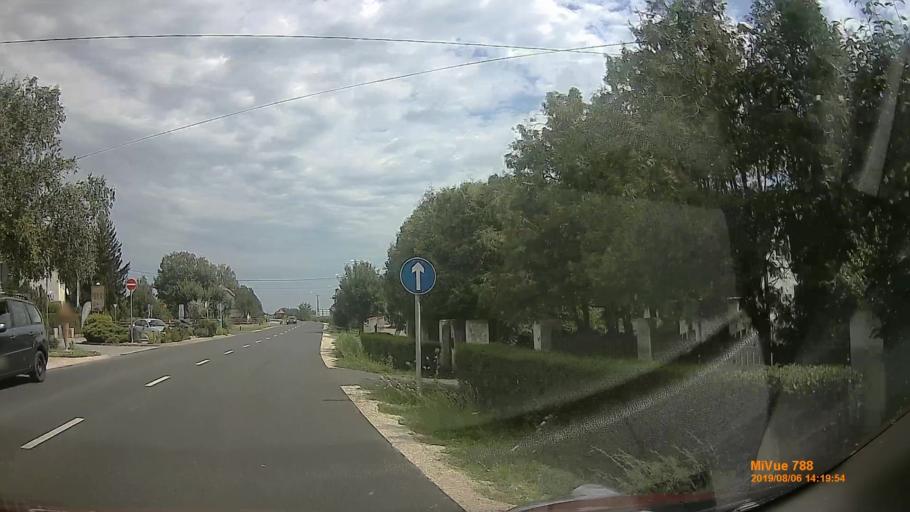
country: HU
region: Vas
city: Taplanszentkereszt
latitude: 47.1793
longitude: 16.7525
